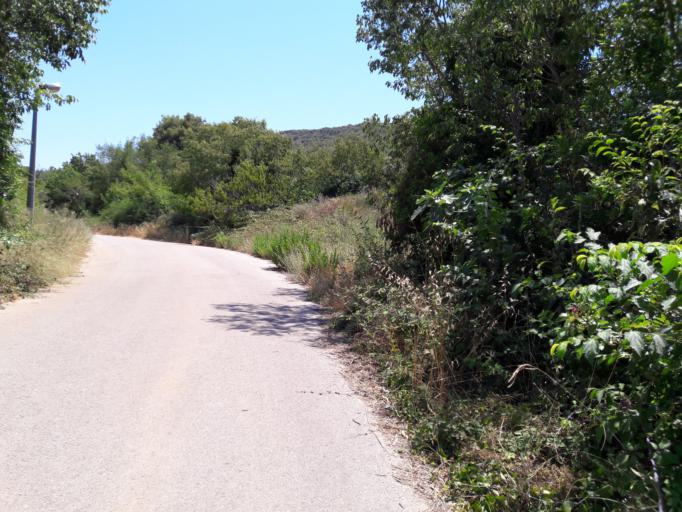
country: HR
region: Sibensko-Kniniska
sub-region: Grad Sibenik
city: Sibenik
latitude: 43.6949
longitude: 15.8389
